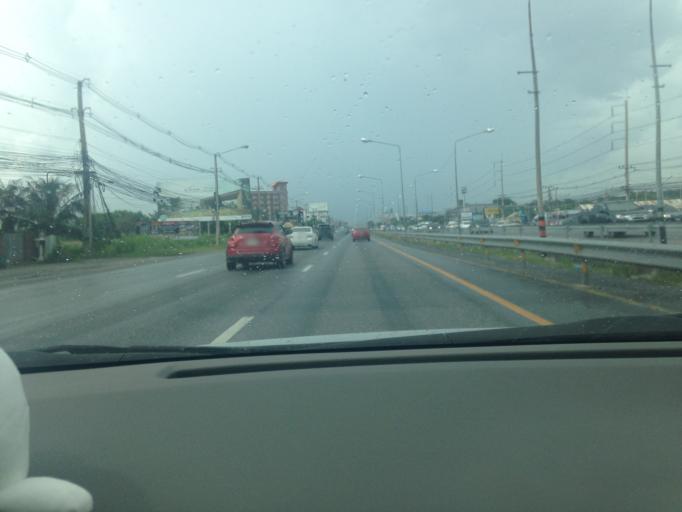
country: TH
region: Chon Buri
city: Chon Buri
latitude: 13.2997
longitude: 100.9477
